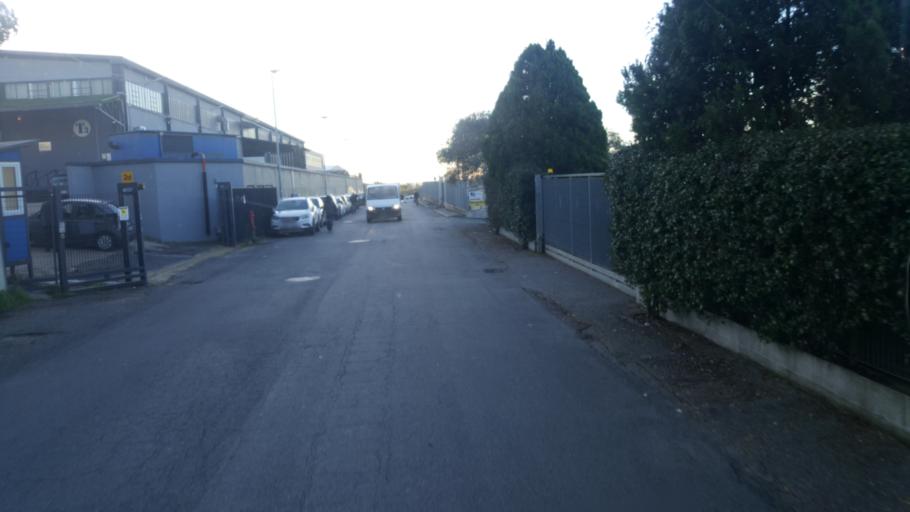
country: IT
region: Latium
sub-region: Citta metropolitana di Roma Capitale
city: Formello
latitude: 42.0518
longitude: 12.4027
